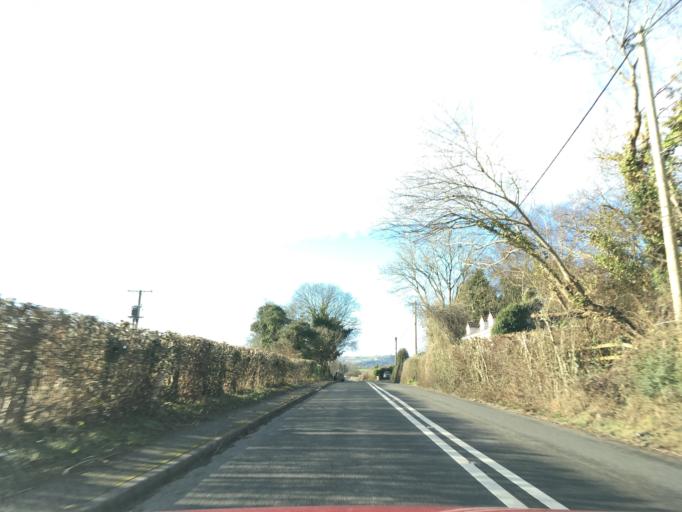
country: GB
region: Wales
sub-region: Monmouthshire
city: Usk
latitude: 51.7190
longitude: -2.9458
